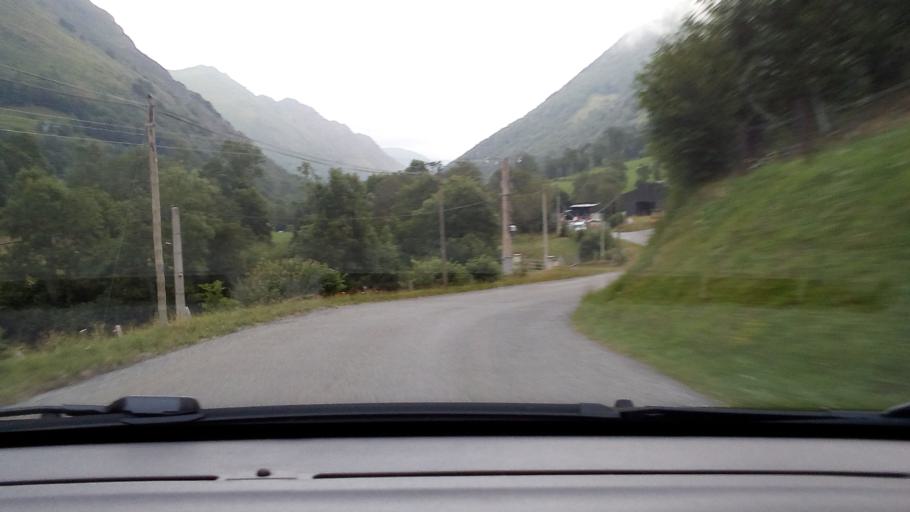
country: FR
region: Midi-Pyrenees
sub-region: Departement des Hautes-Pyrenees
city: Cauterets
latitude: 42.9206
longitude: -0.1857
